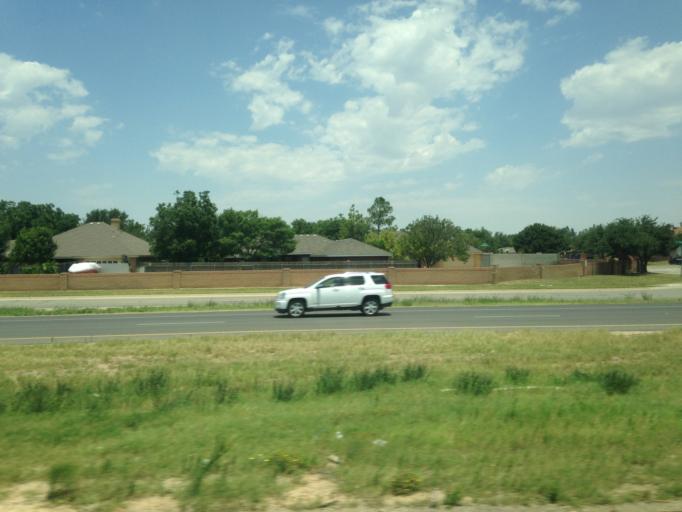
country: US
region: Texas
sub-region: Midland County
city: Midland
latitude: 32.0408
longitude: -102.1002
